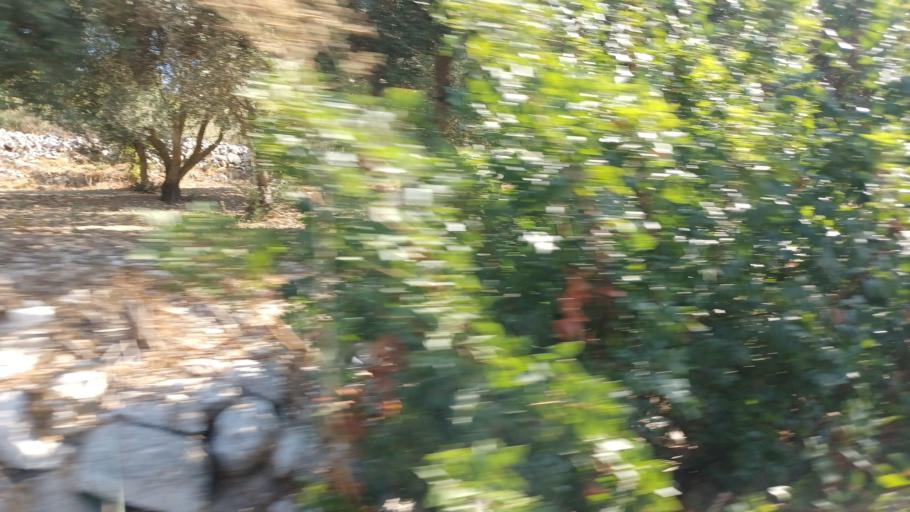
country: CY
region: Pafos
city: Pegeia
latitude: 34.9048
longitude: 32.4240
